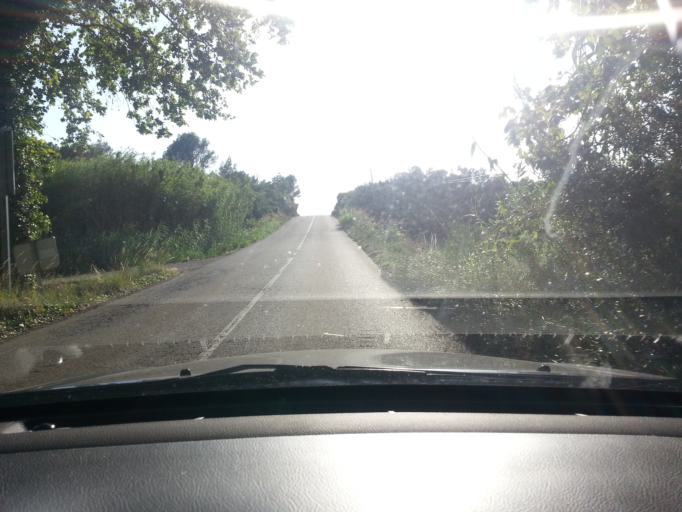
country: ES
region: Catalonia
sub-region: Provincia de Girona
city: Pals
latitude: 42.0121
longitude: 3.1650
